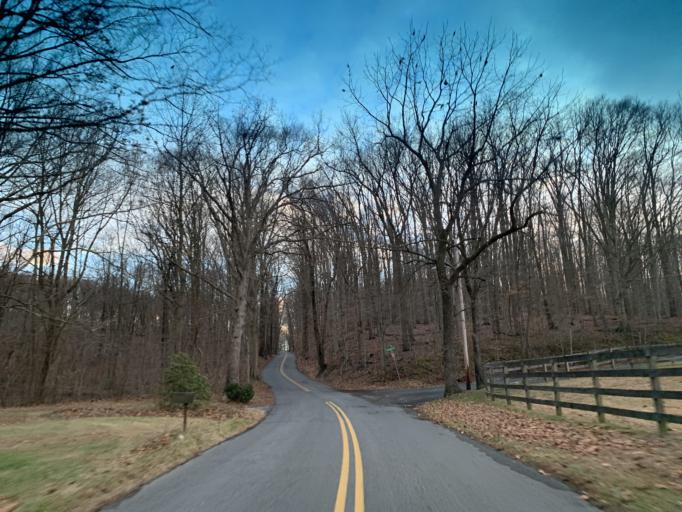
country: US
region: Maryland
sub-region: Harford County
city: Bel Air North
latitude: 39.6060
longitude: -76.3205
